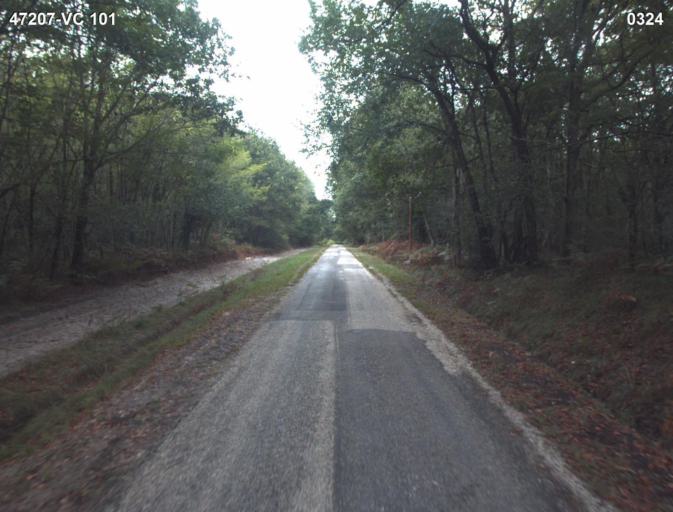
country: FR
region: Aquitaine
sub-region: Departement du Lot-et-Garonne
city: Barbaste
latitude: 44.1894
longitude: 0.1991
